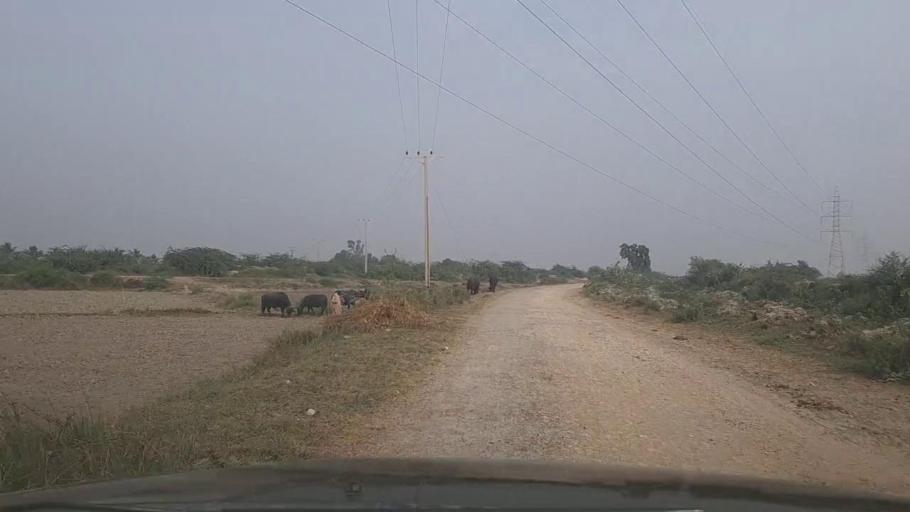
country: PK
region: Sindh
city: Mirpur Sakro
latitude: 24.5726
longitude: 67.7923
